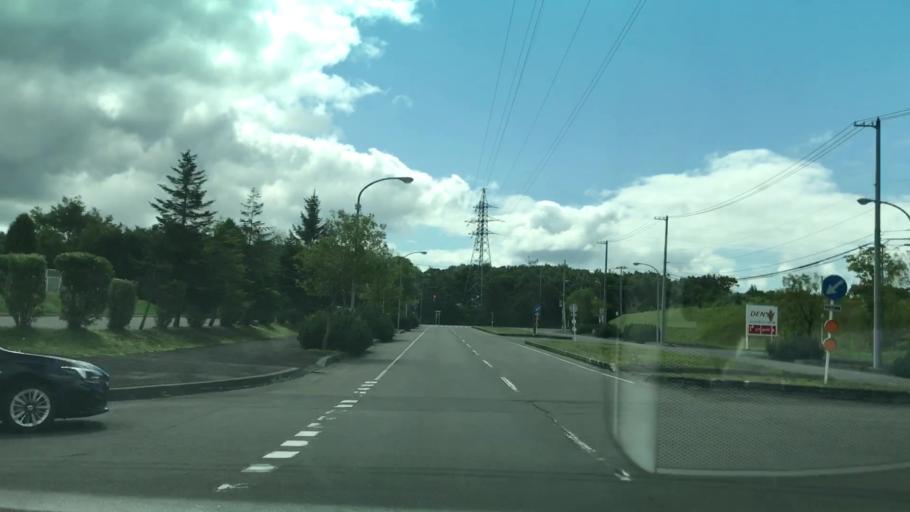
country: JP
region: Hokkaido
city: Chitose
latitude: 42.7740
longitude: 141.6166
